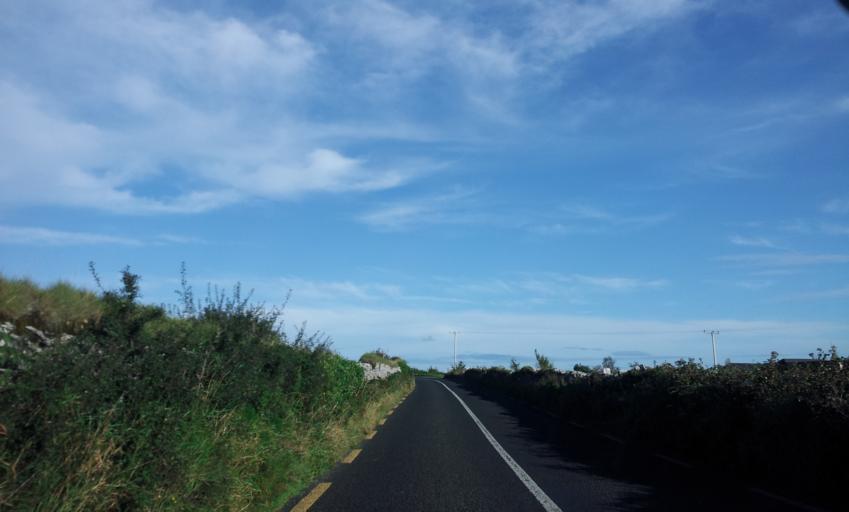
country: IE
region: Munster
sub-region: An Clar
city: Ennis
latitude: 52.9788
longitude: -9.1172
